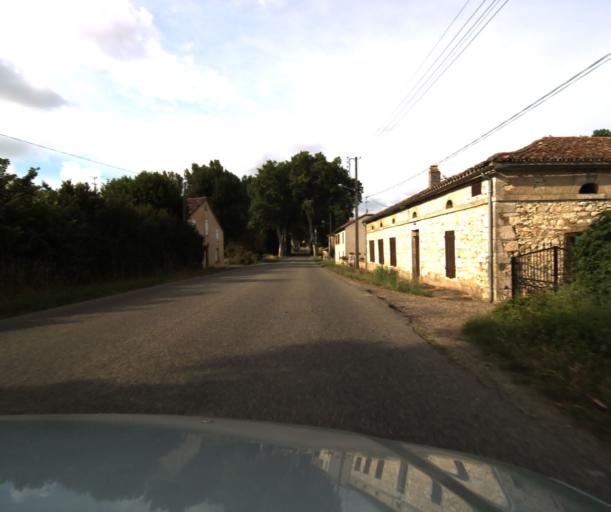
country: FR
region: Midi-Pyrenees
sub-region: Departement du Tarn-et-Garonne
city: Beaumont-de-Lomagne
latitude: 43.8531
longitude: 0.9433
